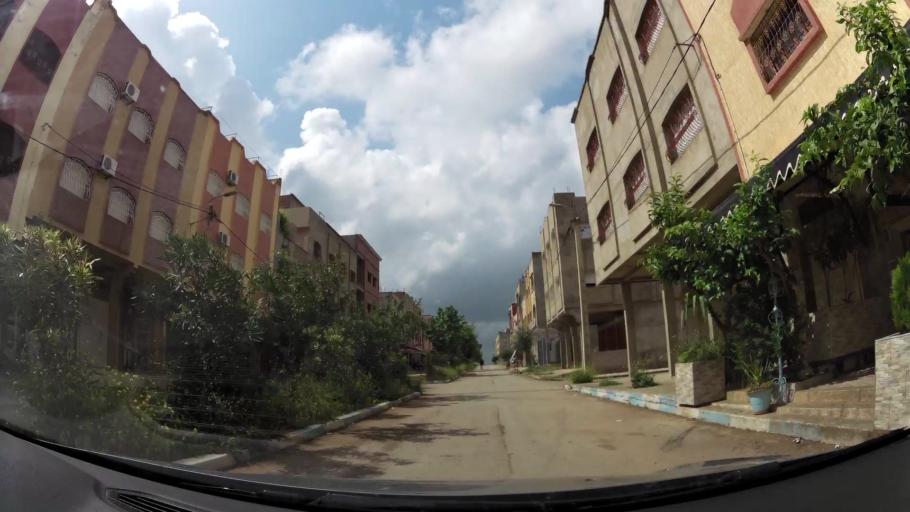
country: MA
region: Rabat-Sale-Zemmour-Zaer
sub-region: Khemisset
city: Tiflet
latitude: 33.8981
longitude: -6.3368
